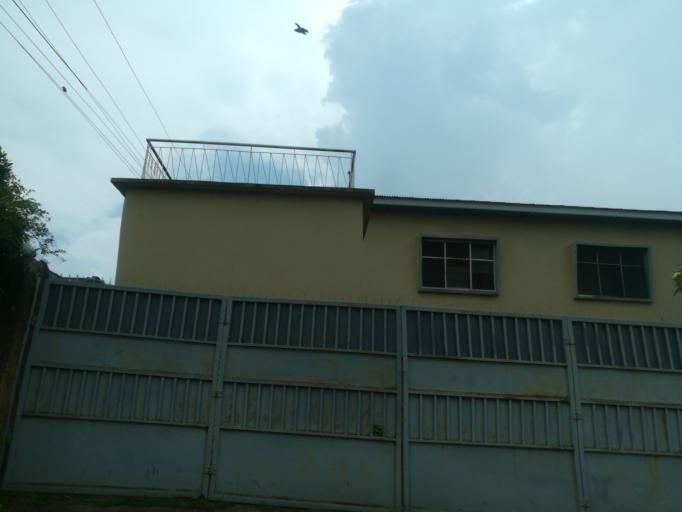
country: NG
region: Oyo
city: Ibadan
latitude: 7.4276
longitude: 3.9131
